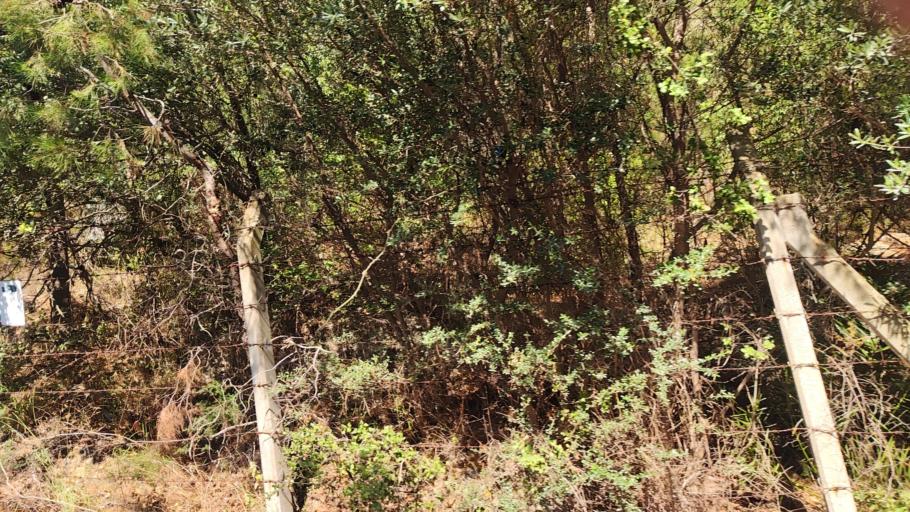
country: TR
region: Mugla
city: Sarigerme
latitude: 36.7071
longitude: 28.6982
